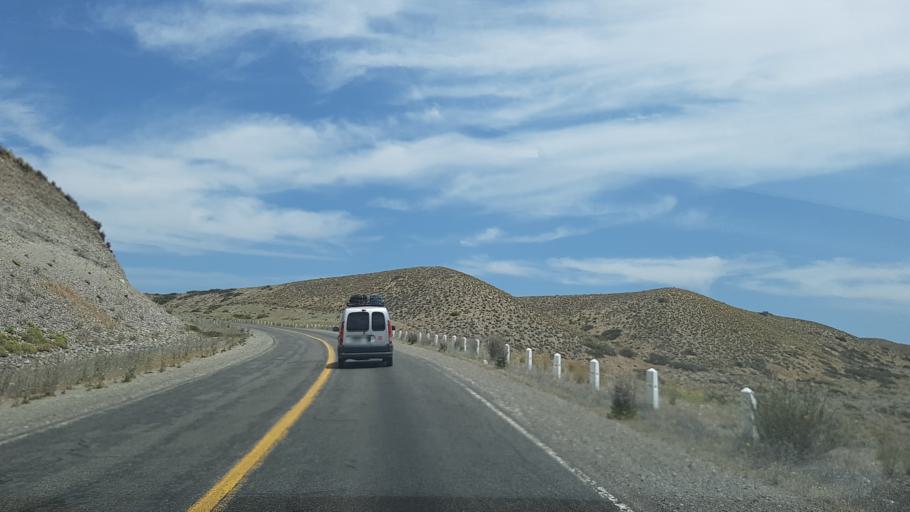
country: AR
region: Rio Negro
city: Pilcaniyeu
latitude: -40.4840
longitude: -70.6786
